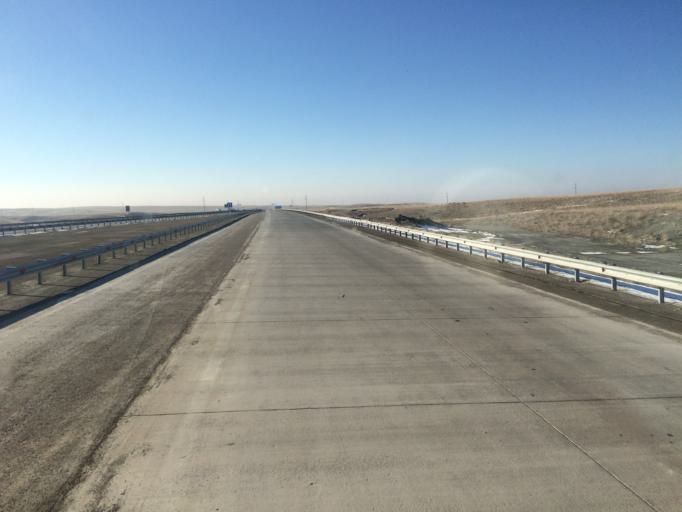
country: KZ
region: Zhambyl
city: Georgiyevka
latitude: 43.3542
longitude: 74.5649
